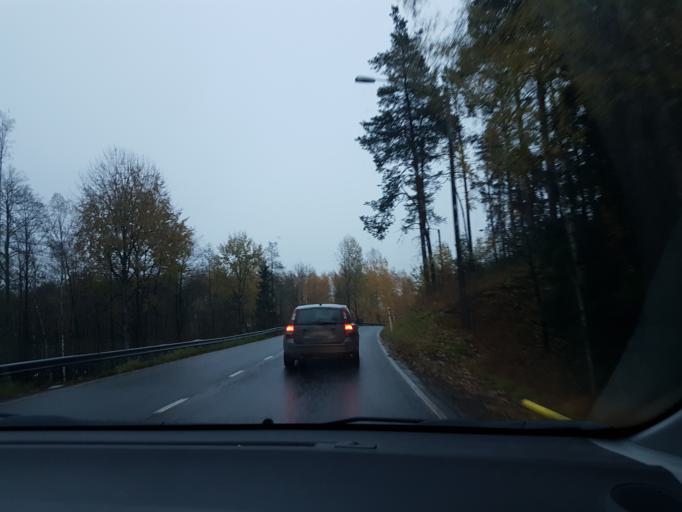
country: FI
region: Uusimaa
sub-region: Helsinki
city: Tuusula
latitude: 60.4044
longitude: 25.0186
